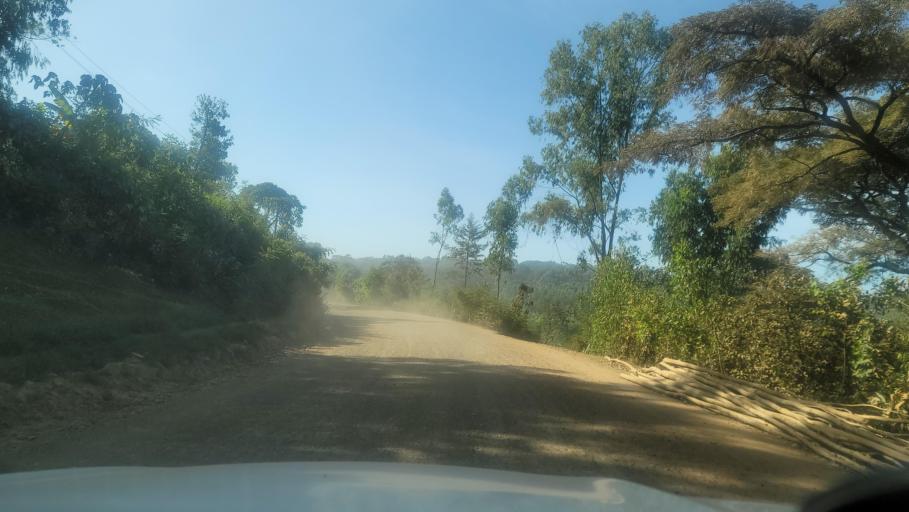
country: ET
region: Oromiya
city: Agaro
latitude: 7.8366
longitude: 36.5419
